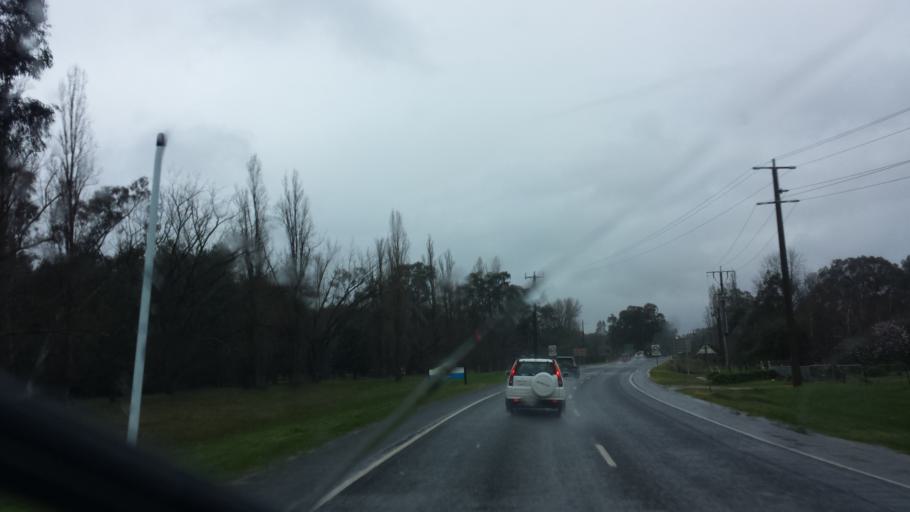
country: AU
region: Victoria
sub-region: Alpine
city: Mount Beauty
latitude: -36.5839
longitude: 146.7564
